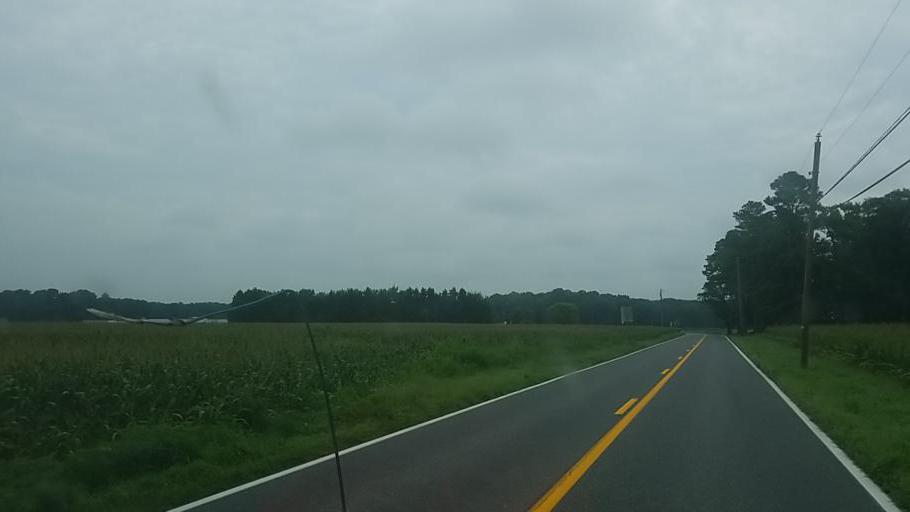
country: US
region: Delaware
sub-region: Sussex County
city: Selbyville
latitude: 38.4501
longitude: -75.1872
